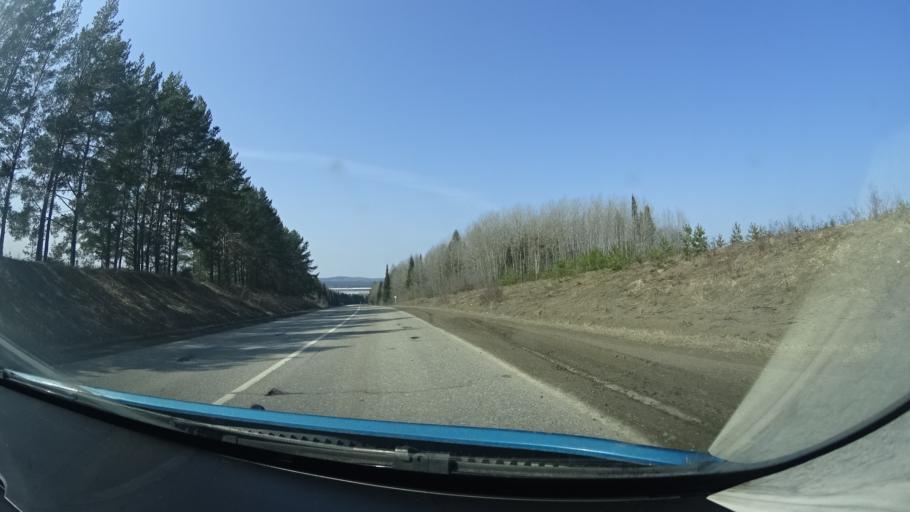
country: RU
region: Perm
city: Osa
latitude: 57.3242
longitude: 55.6116
